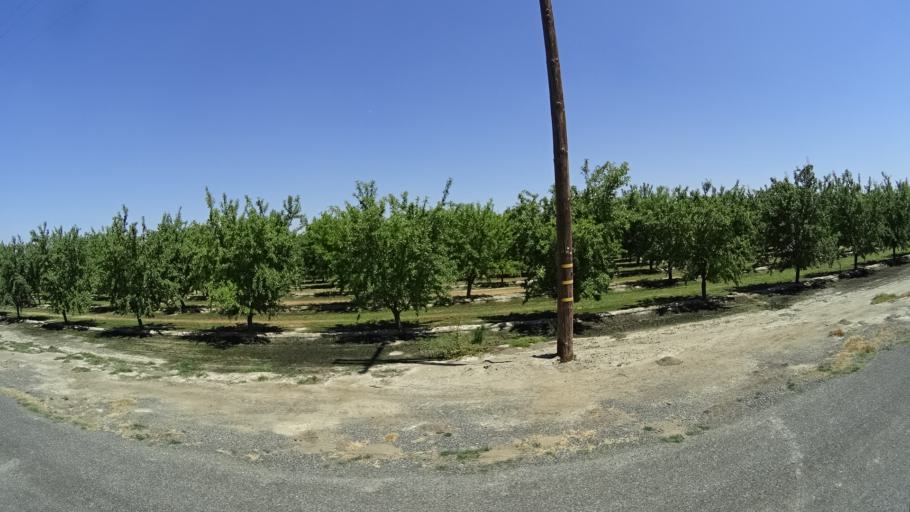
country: US
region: California
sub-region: Fresno County
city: Laton
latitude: 36.4068
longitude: -119.6954
